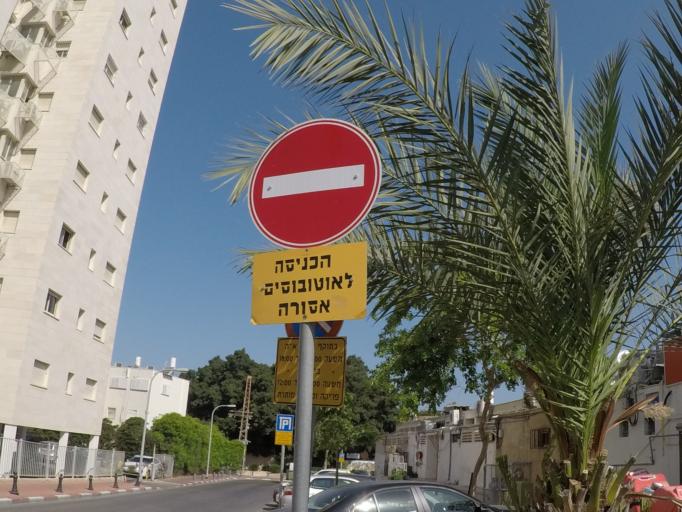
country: IL
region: Tel Aviv
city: Ramat Gan
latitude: 32.1065
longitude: 34.7974
